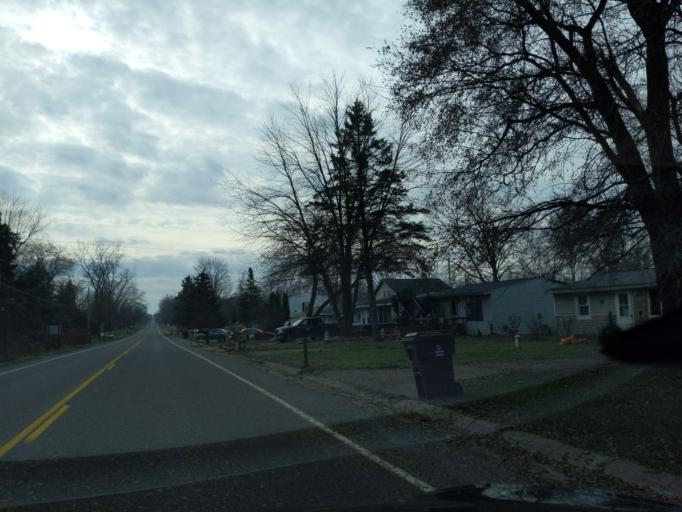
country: US
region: Michigan
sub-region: Ingham County
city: Holt
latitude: 42.5817
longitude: -84.5229
